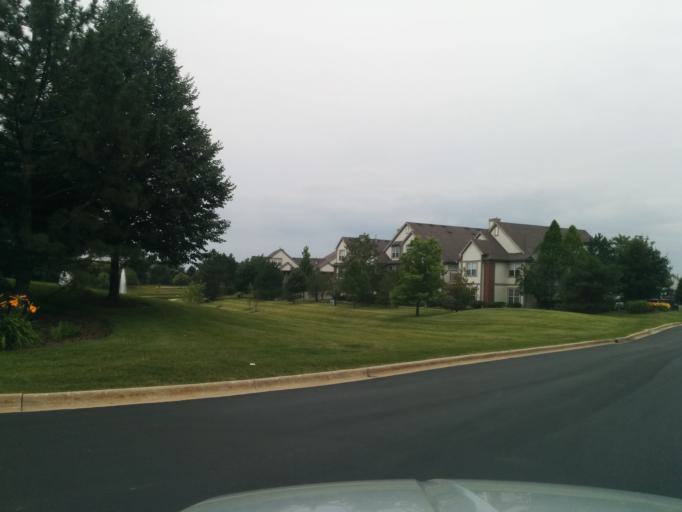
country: US
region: Illinois
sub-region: Kane County
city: Aurora
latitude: 41.7680
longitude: -88.2438
